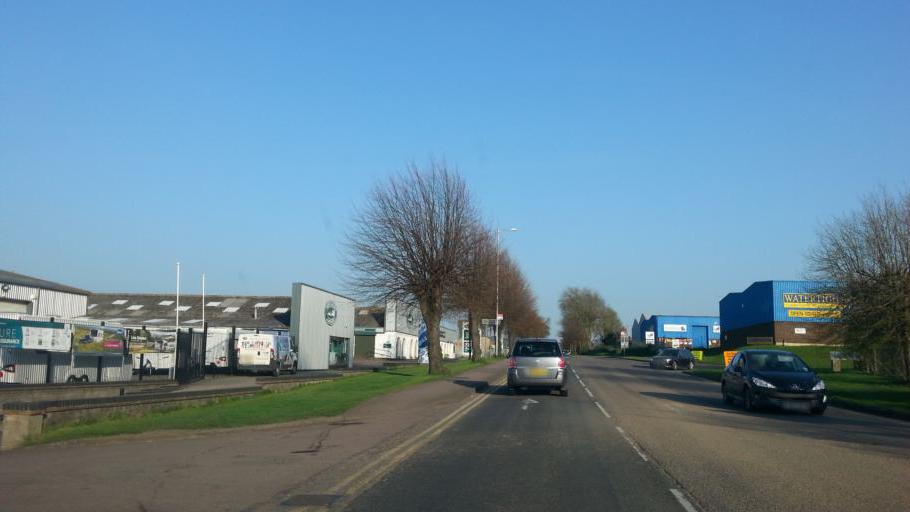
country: GB
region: England
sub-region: Northamptonshire
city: Rushden
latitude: 52.2972
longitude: -0.6251
